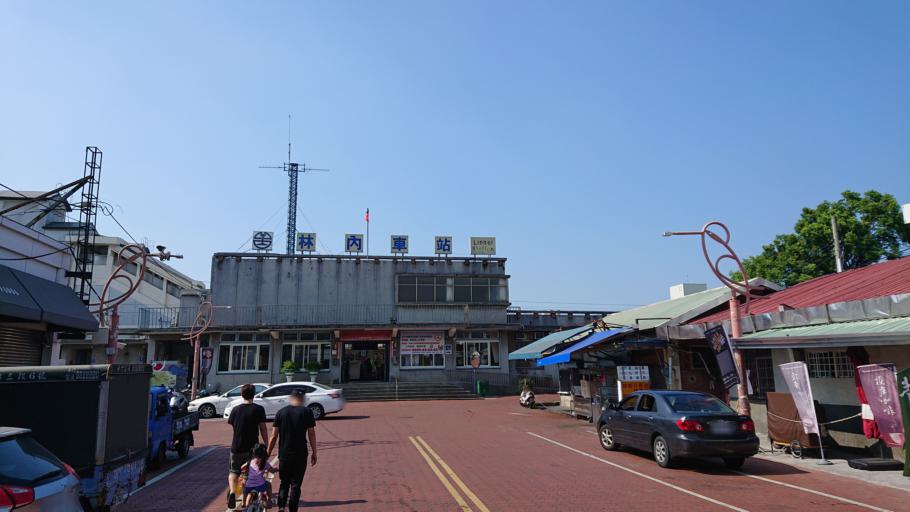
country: TW
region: Taiwan
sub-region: Yunlin
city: Douliu
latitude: 23.7594
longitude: 120.6152
